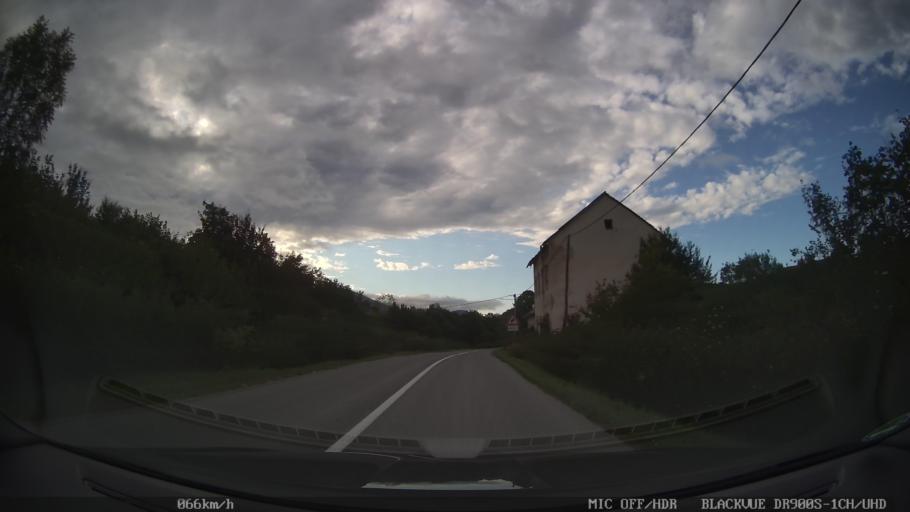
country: HR
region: Karlovacka
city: Plaski
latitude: 44.9946
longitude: 15.4451
